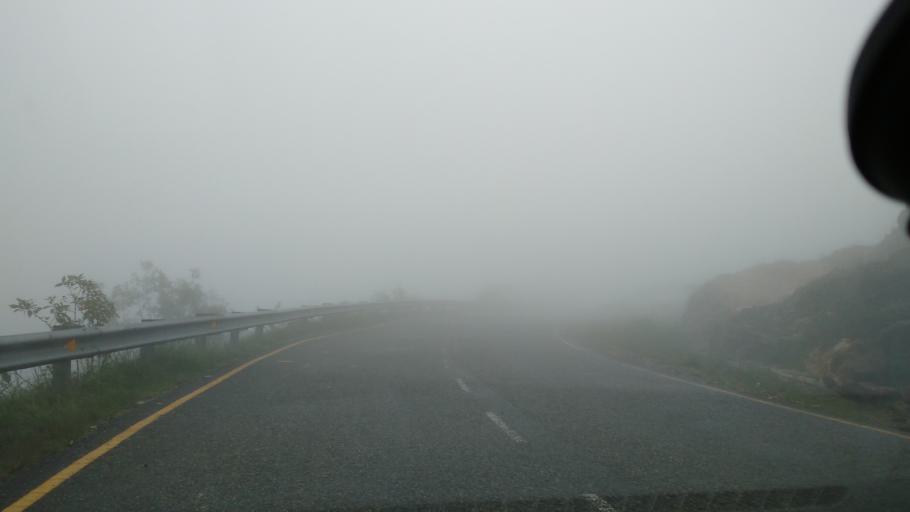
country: IN
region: Meghalaya
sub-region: East Khasi Hills
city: Cherrapunji
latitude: 25.3129
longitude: 91.7301
